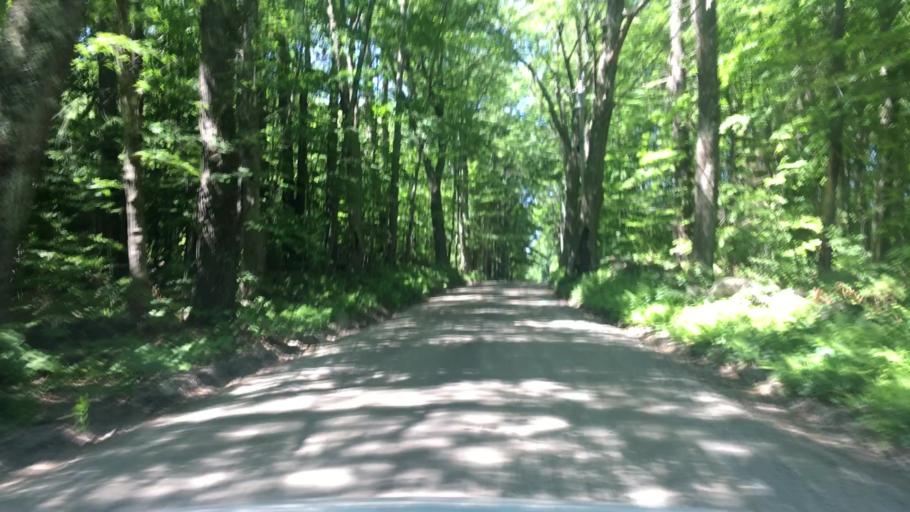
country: US
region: New Hampshire
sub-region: Merrimack County
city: Contoocook
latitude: 43.2285
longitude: -71.6776
